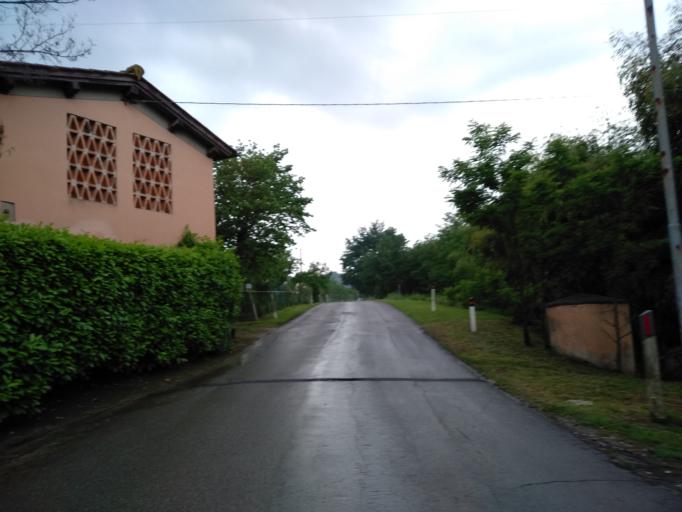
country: IT
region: Tuscany
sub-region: Province of Arezzo
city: San Giovanni Valdarno
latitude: 43.5579
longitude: 11.5244
